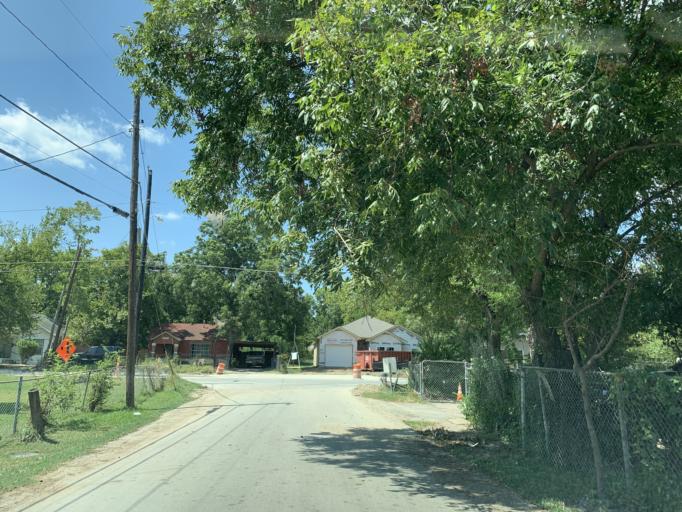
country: US
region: Texas
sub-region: Dallas County
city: Dallas
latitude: 32.7120
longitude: -96.7704
